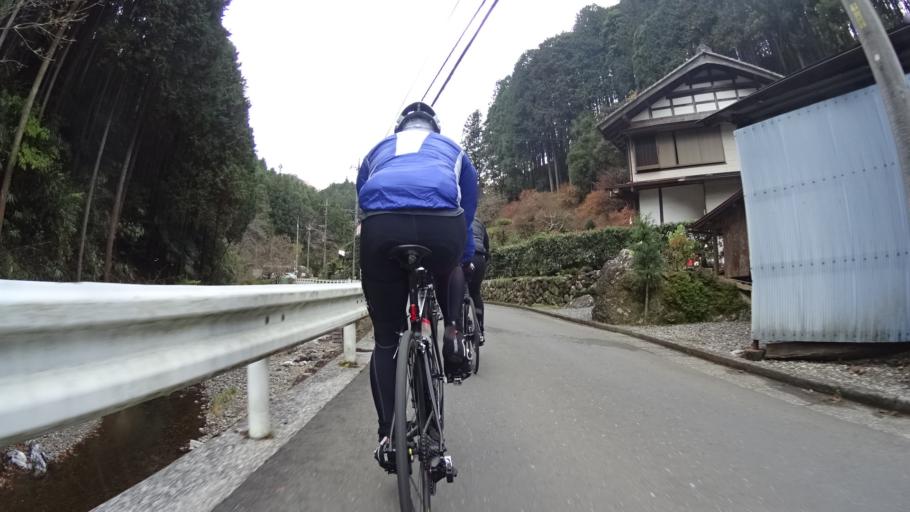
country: JP
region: Saitama
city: Morohongo
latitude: 35.9233
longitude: 139.1902
